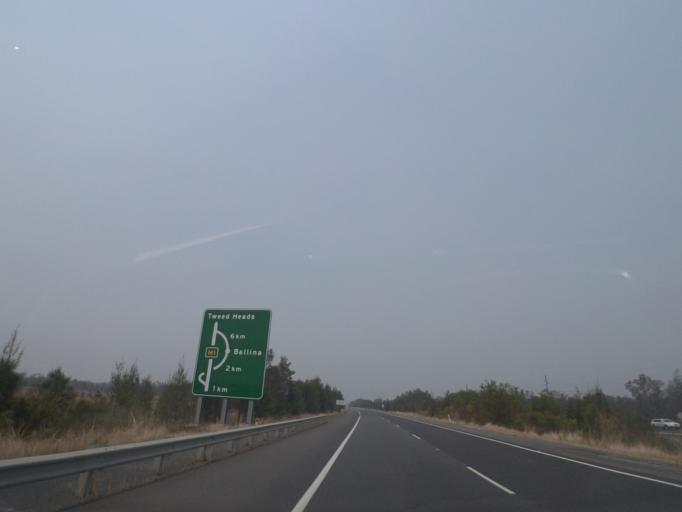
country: AU
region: New South Wales
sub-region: Ballina
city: Ballina
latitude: -28.8648
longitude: 153.5069
